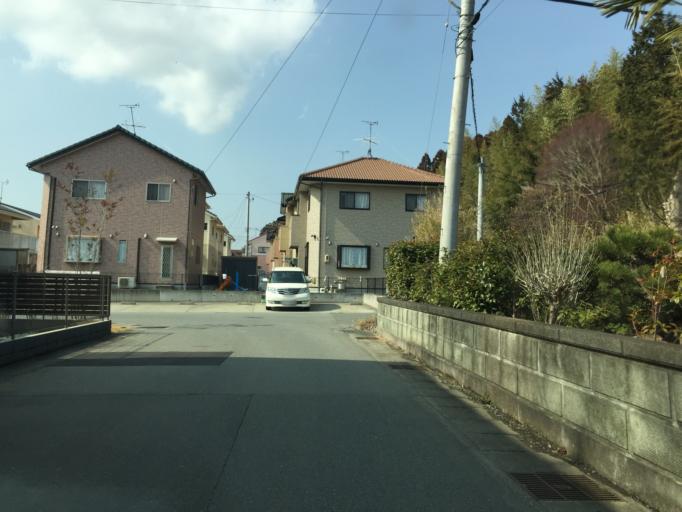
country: JP
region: Ibaraki
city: Kitaibaraki
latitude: 36.9202
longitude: 140.8096
